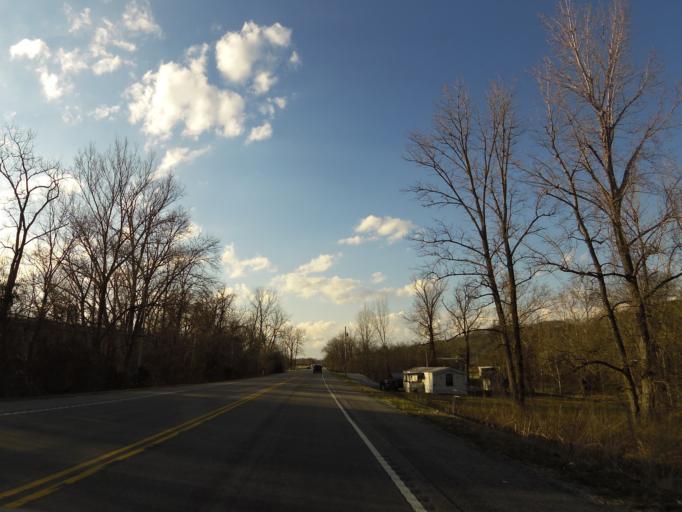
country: US
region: Tennessee
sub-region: Smith County
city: Carthage
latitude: 36.2558
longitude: -86.0453
